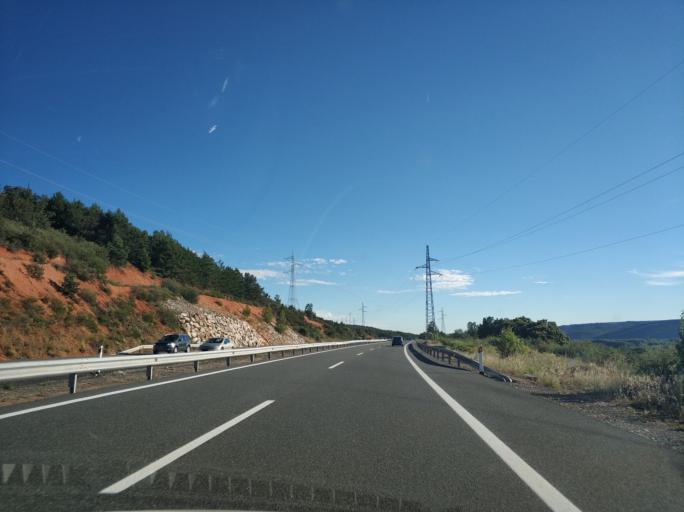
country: ES
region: Castille and Leon
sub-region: Provincia de Leon
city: Santa Maria de Ordas
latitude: 42.7212
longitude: -5.7913
